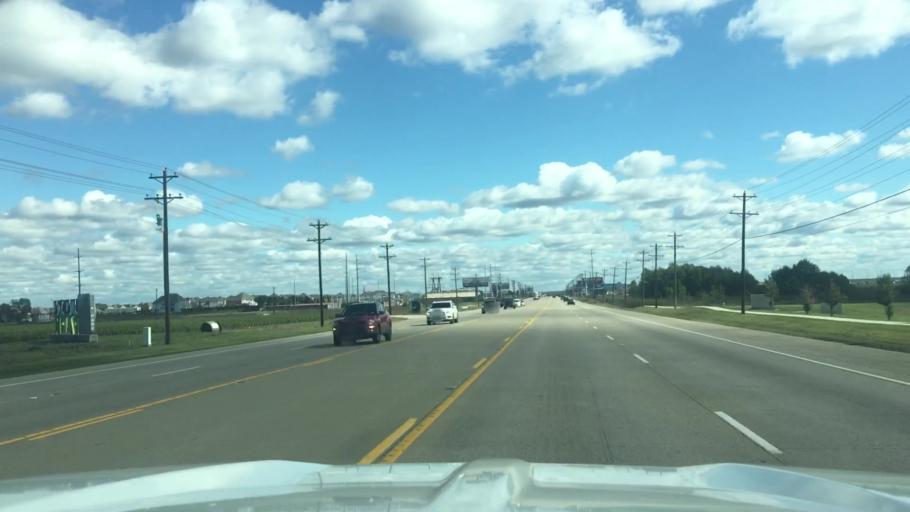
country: US
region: Texas
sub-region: Denton County
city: Little Elm
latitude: 33.2205
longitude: -96.9242
